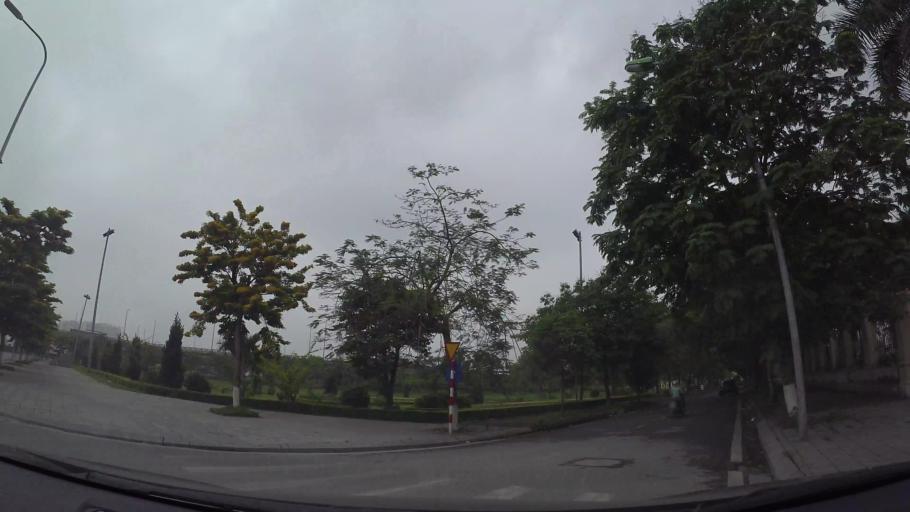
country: VN
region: Ha Noi
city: Van Dien
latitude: 20.9675
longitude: 105.8490
